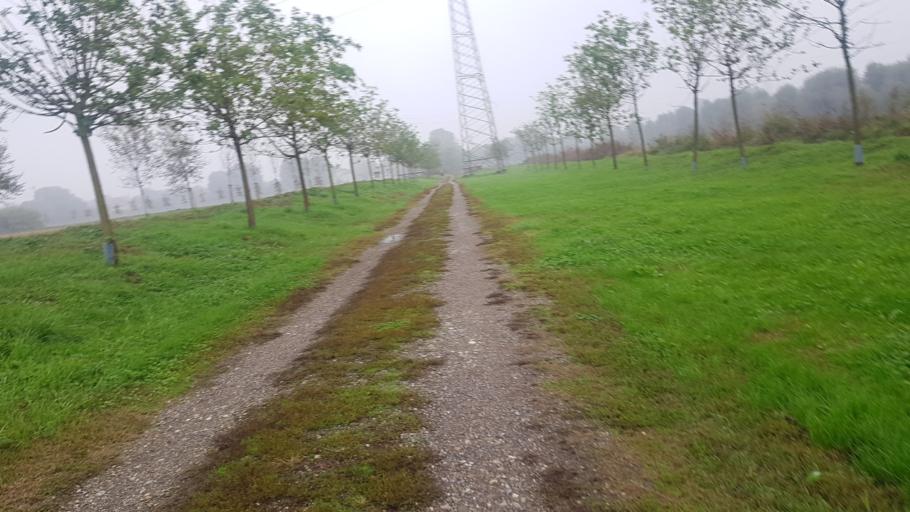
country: IT
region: Lombardy
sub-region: Citta metropolitana di Milano
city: Chiaravalle
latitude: 45.4184
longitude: 9.2285
